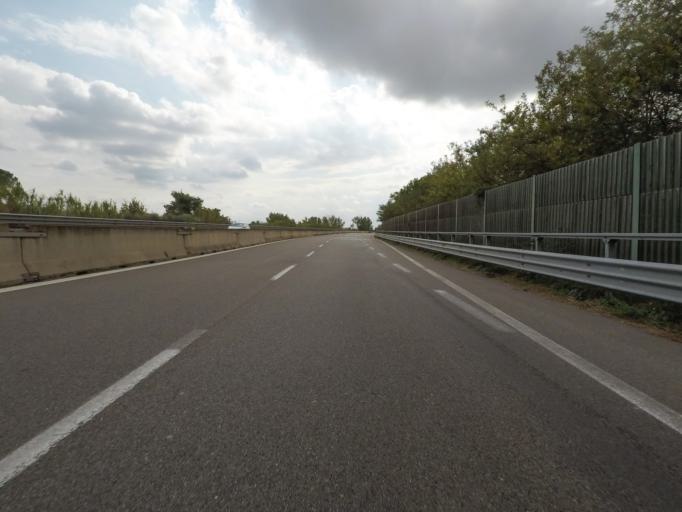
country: IT
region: Tuscany
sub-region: Provincia di Grosseto
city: Bagno Roselle
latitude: 42.8043
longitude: 11.1343
